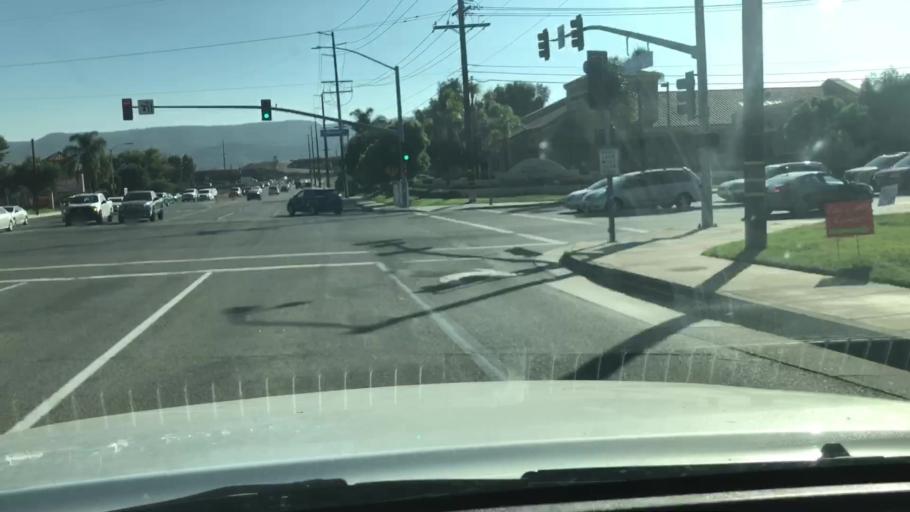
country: US
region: California
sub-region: Riverside County
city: Murrieta
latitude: 33.5533
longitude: -117.1956
